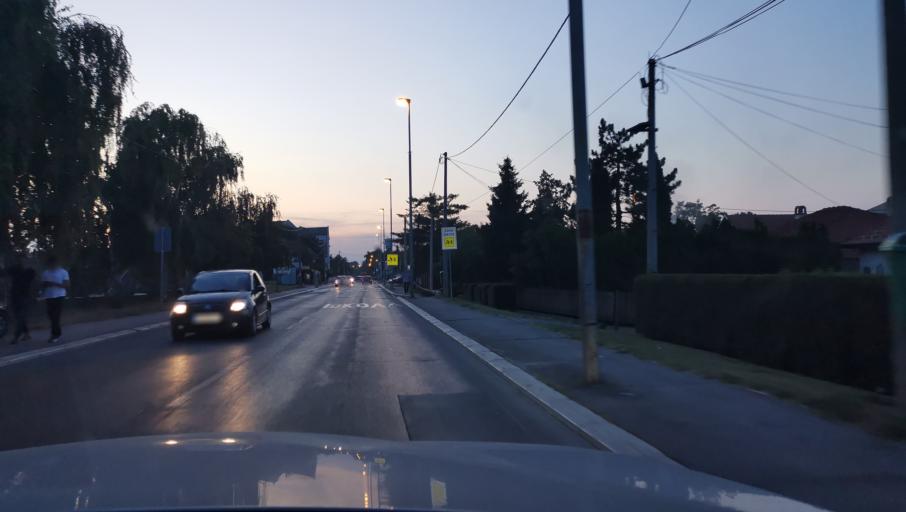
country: RS
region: Central Serbia
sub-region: Belgrade
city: Obrenovac
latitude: 44.6662
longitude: 20.1948
